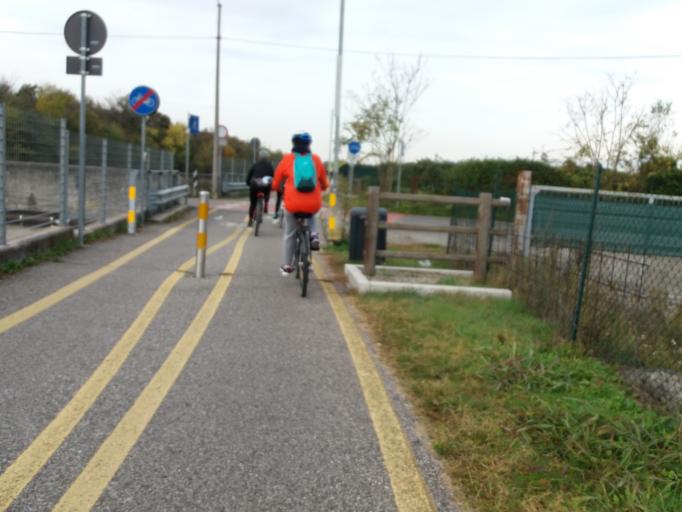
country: IT
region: Veneto
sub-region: Provincia di Verona
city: Settimo
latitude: 45.4655
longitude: 10.9174
